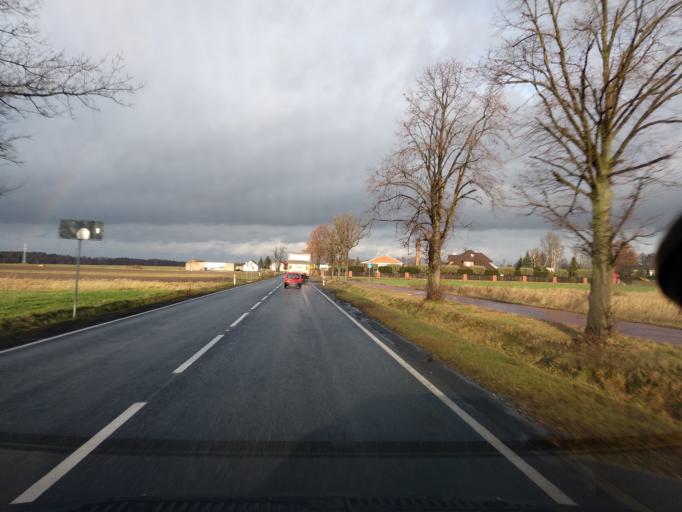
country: PL
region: Greater Poland Voivodeship
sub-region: Powiat koninski
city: Rychwal
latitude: 52.1131
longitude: 18.1676
